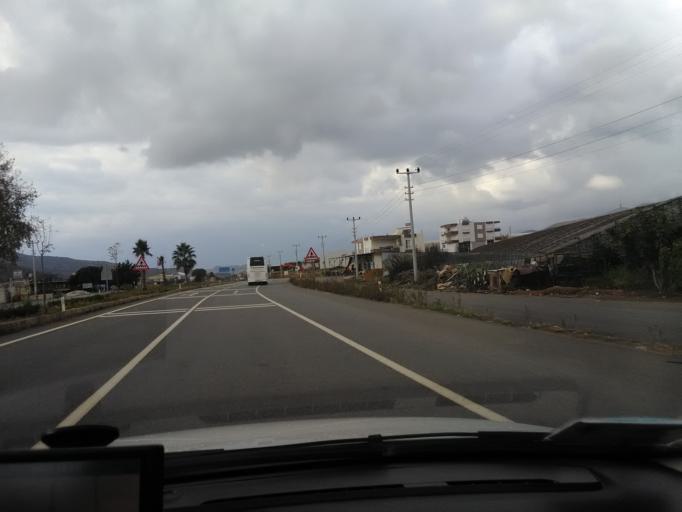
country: TR
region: Antalya
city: Gazipasa
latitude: 36.2267
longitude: 32.3825
